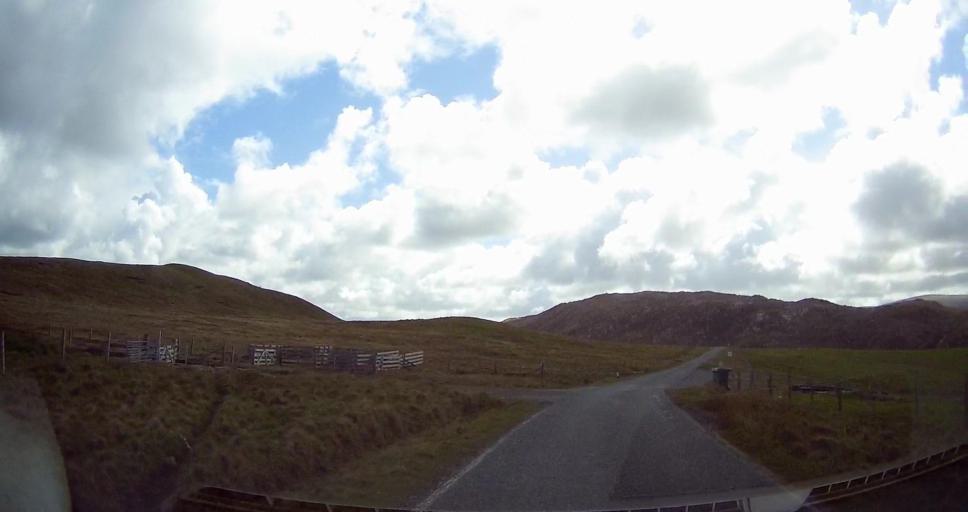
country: GB
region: Scotland
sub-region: Shetland Islands
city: Lerwick
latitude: 60.5587
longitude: -1.3363
